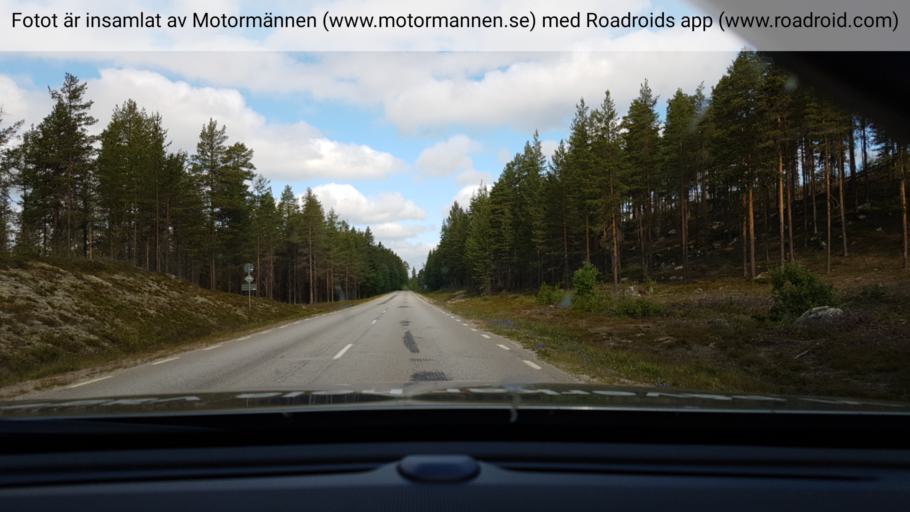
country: SE
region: Vaesterbotten
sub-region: Norsjo Kommun
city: Norsjoe
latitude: 64.7551
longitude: 19.0803
